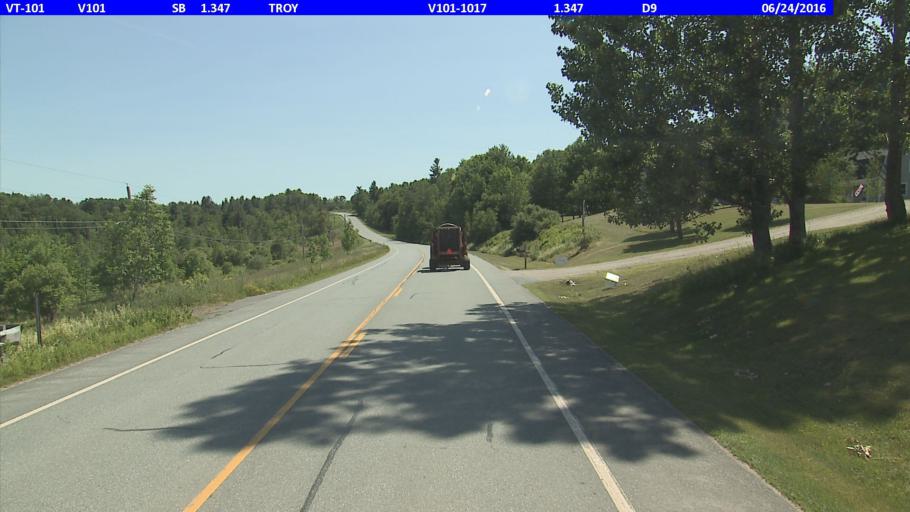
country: US
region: Vermont
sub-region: Orleans County
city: Newport
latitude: 44.9225
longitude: -72.4088
